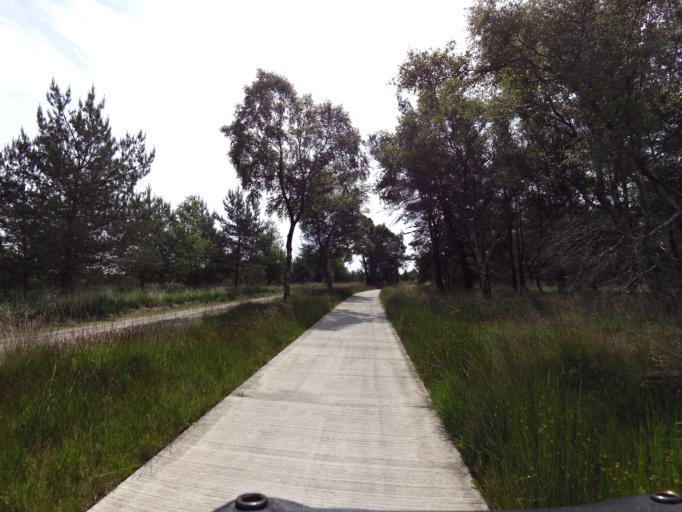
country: NL
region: Gelderland
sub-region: Gemeente Rozendaal
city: Rozendaal
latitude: 52.0467
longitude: 5.9835
